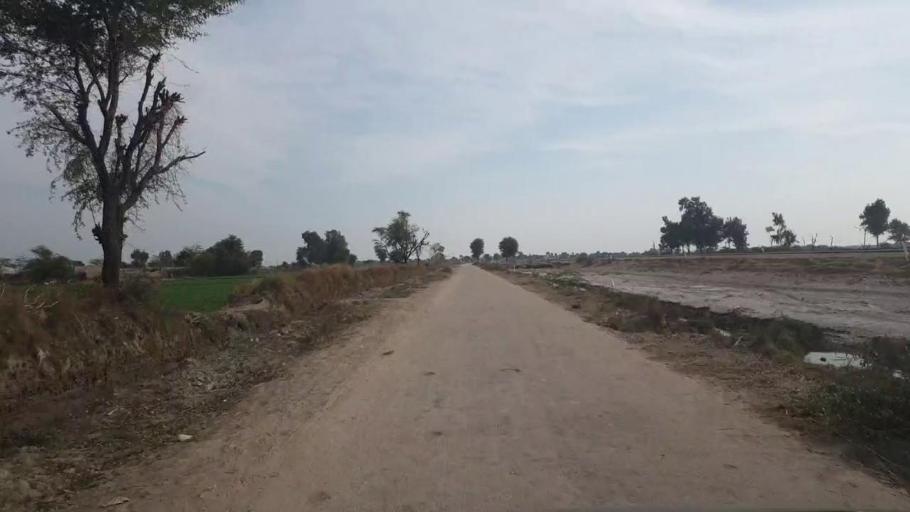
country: PK
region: Sindh
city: Nawabshah
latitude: 26.0886
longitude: 68.4857
